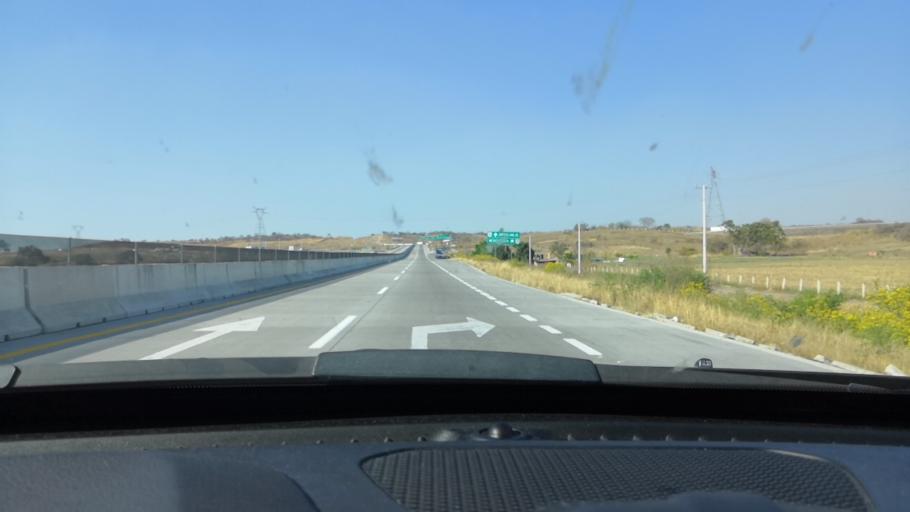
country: MX
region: Jalisco
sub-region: Zapotlanejo
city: La Mezquitera
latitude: 20.5797
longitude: -103.1002
